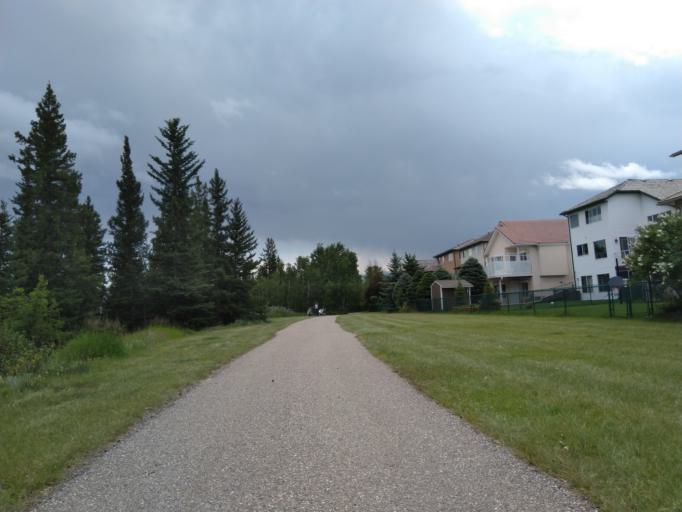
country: CA
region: Alberta
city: Cochrane
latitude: 51.1893
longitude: -114.5106
